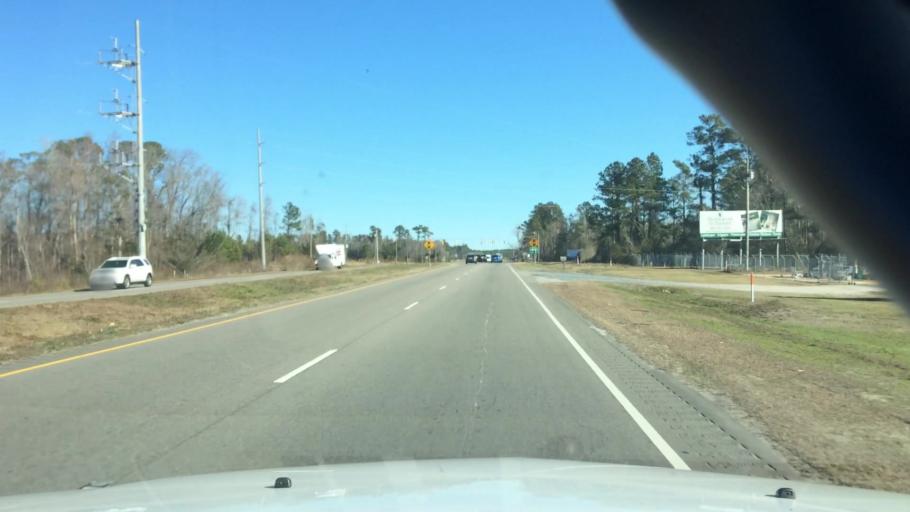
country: US
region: North Carolina
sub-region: Brunswick County
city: Bolivia
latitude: 34.0244
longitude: -78.2625
